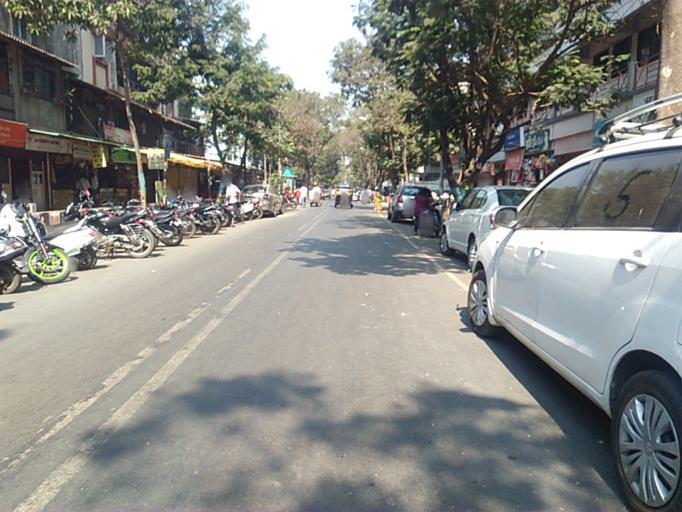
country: IN
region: Maharashtra
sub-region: Thane
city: Bhayandar
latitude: 19.3141
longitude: 72.8543
